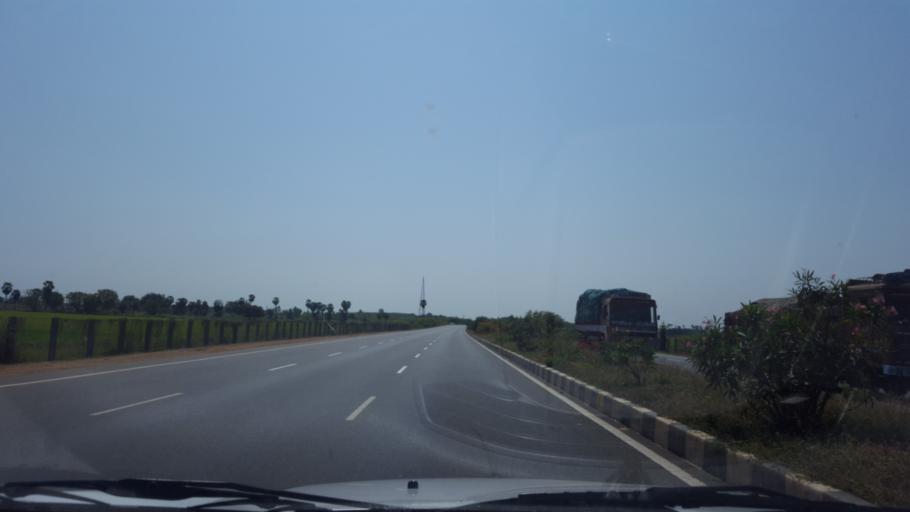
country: IN
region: Andhra Pradesh
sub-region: Prakasam
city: Singarayakonda
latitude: 15.1016
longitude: 80.0079
